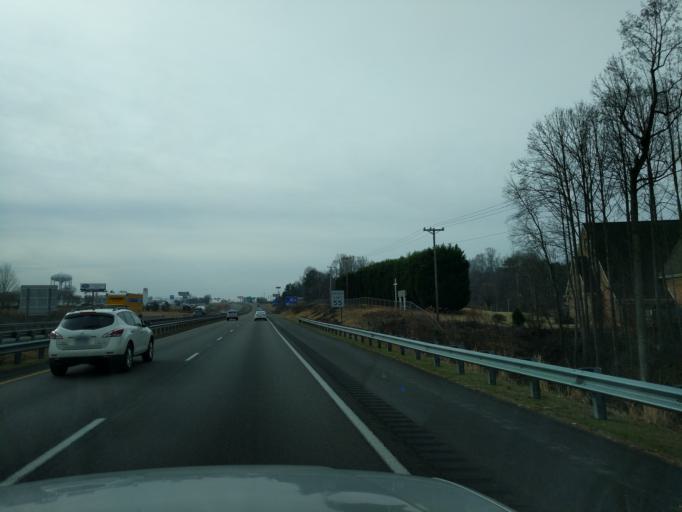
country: US
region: North Carolina
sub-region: Iredell County
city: Statesville
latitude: 35.7841
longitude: -80.8633
